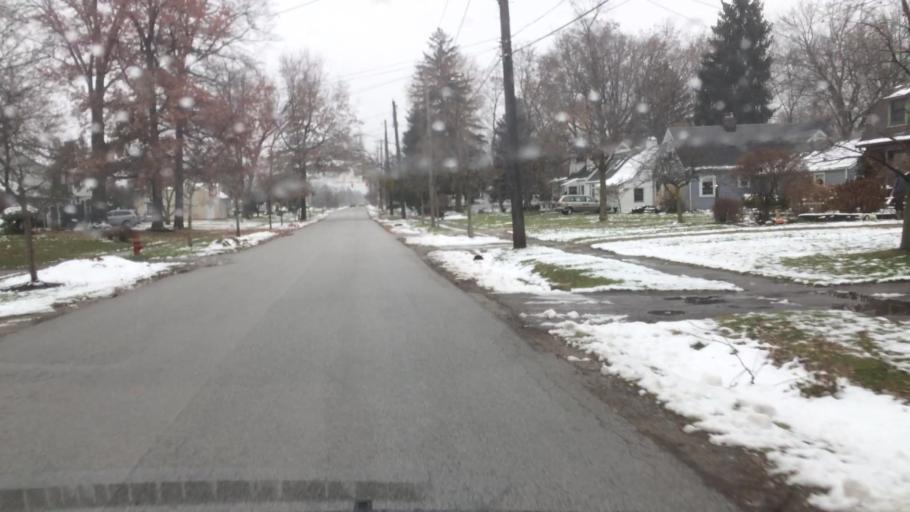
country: US
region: Ohio
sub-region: Cuyahoga County
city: Olmsted Falls
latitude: 41.3712
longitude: -81.9095
